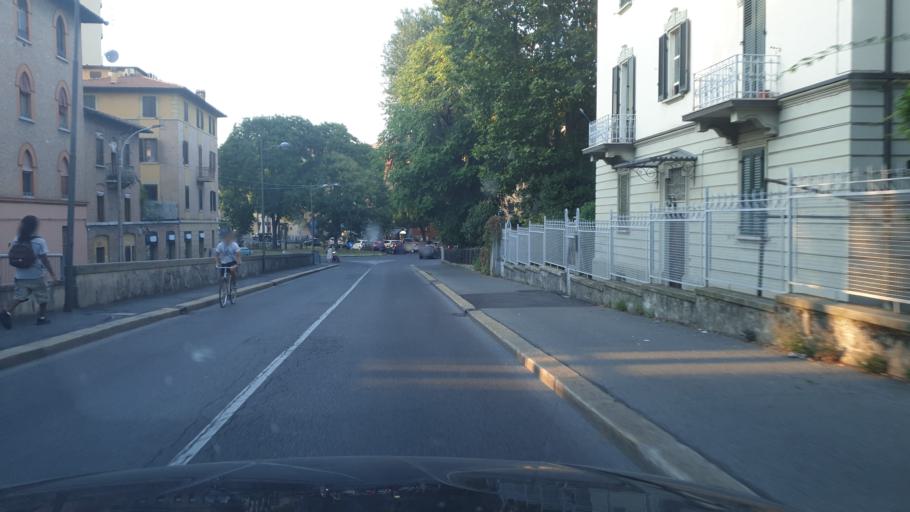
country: IT
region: Emilia-Romagna
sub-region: Provincia di Bologna
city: Bologna
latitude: 44.5010
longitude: 11.3654
